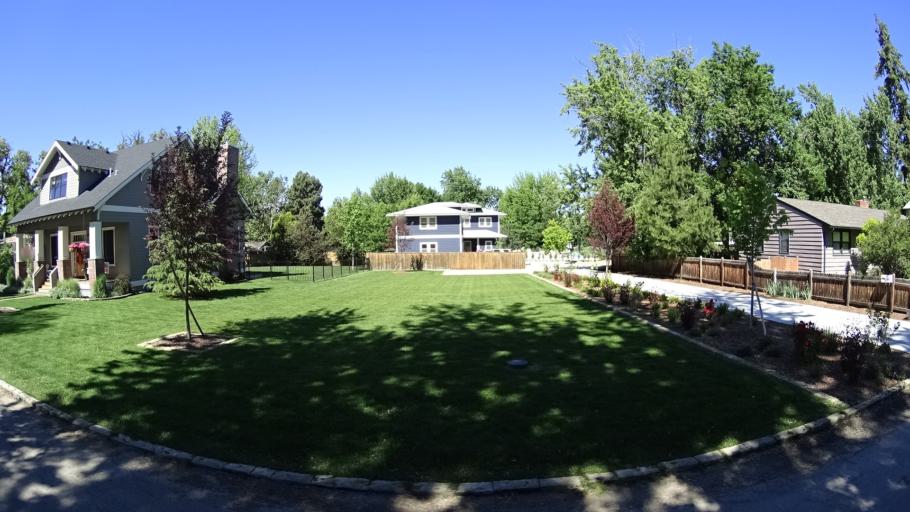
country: US
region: Idaho
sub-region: Ada County
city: Boise
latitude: 43.6386
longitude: -116.2134
